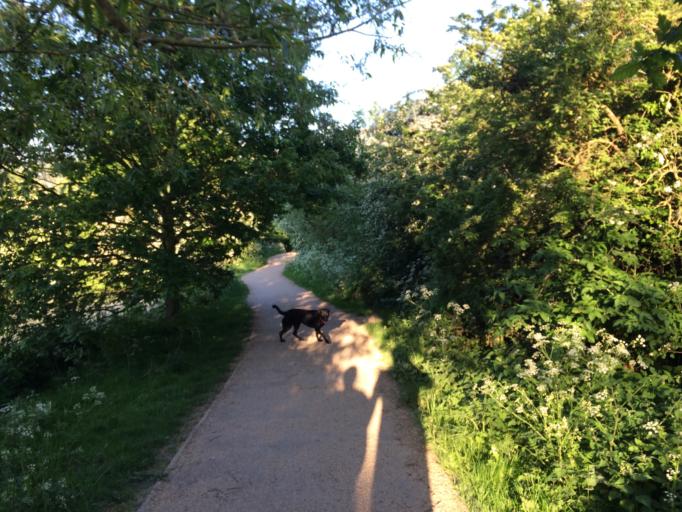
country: GB
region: England
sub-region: Nottinghamshire
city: Gotham
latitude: 52.9019
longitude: -1.2230
